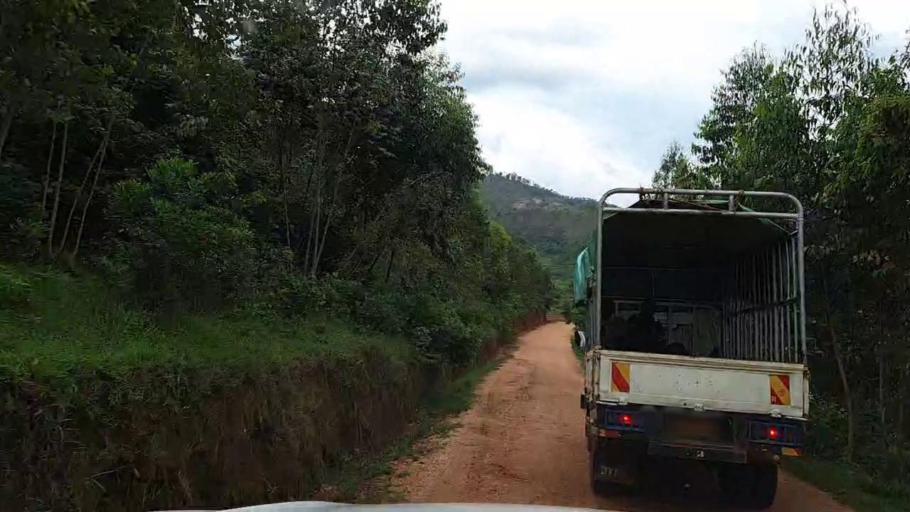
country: RW
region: Southern Province
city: Nyanza
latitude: -2.3925
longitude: 29.6823
